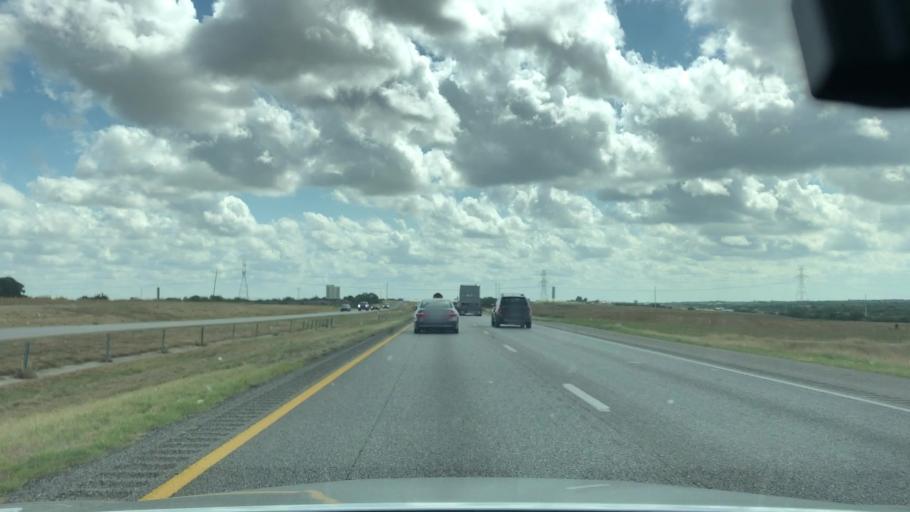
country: US
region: Texas
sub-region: Guadalupe County
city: McQueeney
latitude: 29.5423
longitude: -98.0668
